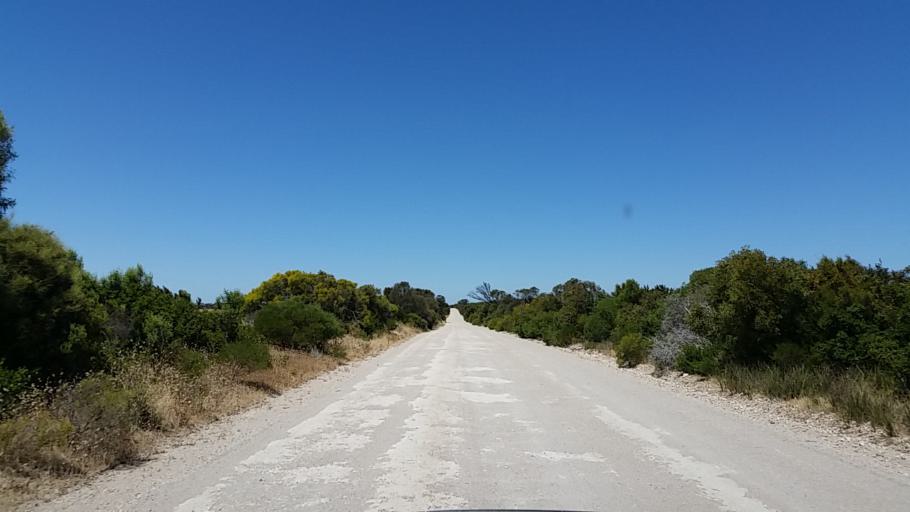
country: AU
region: South Australia
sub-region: Yorke Peninsula
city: Honiton
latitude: -35.0930
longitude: 137.4381
